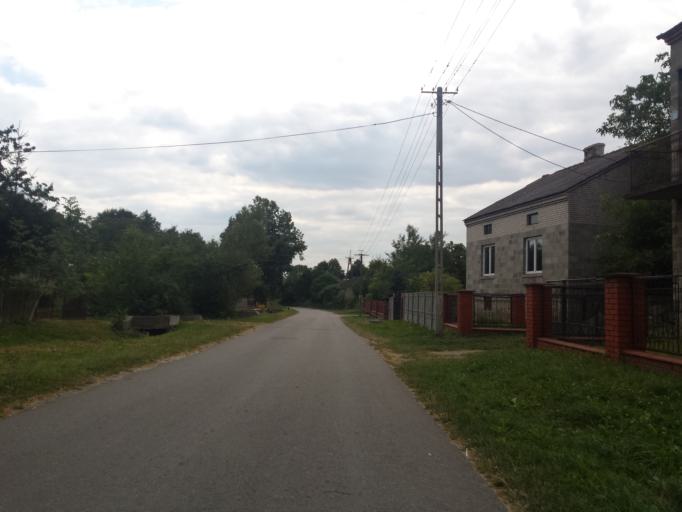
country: PL
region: Swietokrzyskie
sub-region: Powiat staszowski
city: Bogoria
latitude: 50.6638
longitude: 21.2352
